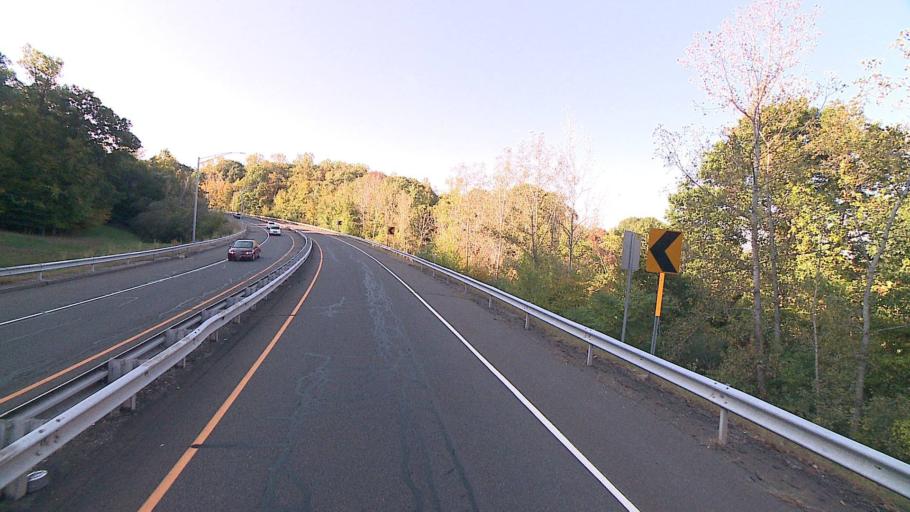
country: US
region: Connecticut
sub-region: New Haven County
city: City of Milford (balance)
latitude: 41.2500
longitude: -73.0858
